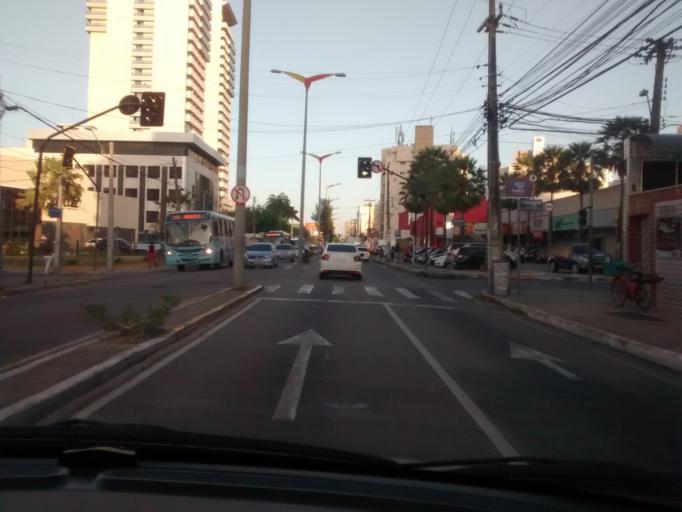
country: BR
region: Ceara
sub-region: Fortaleza
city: Fortaleza
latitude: -3.7416
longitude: -38.4818
